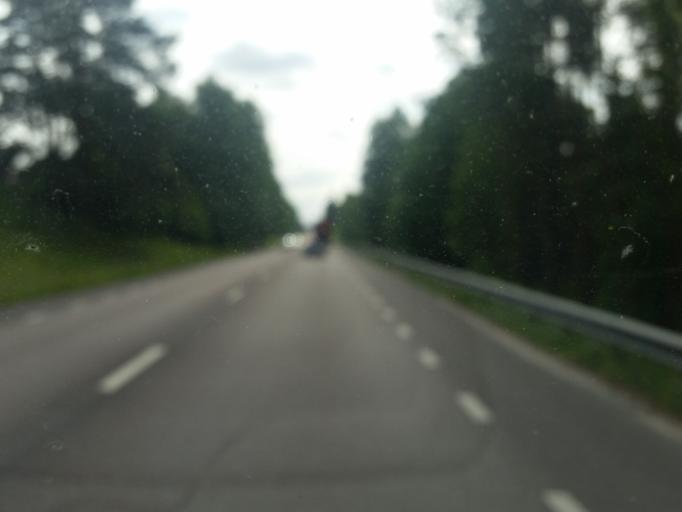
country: SE
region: Dalarna
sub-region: Gagnefs Kommun
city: Gagnef
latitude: 60.5989
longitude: 15.0725
